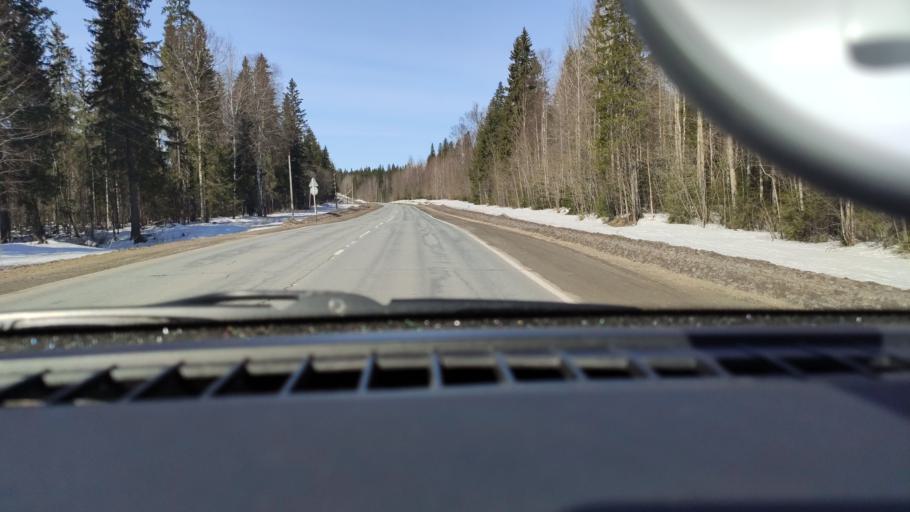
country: RU
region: Perm
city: Perm
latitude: 58.1989
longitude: 56.2073
